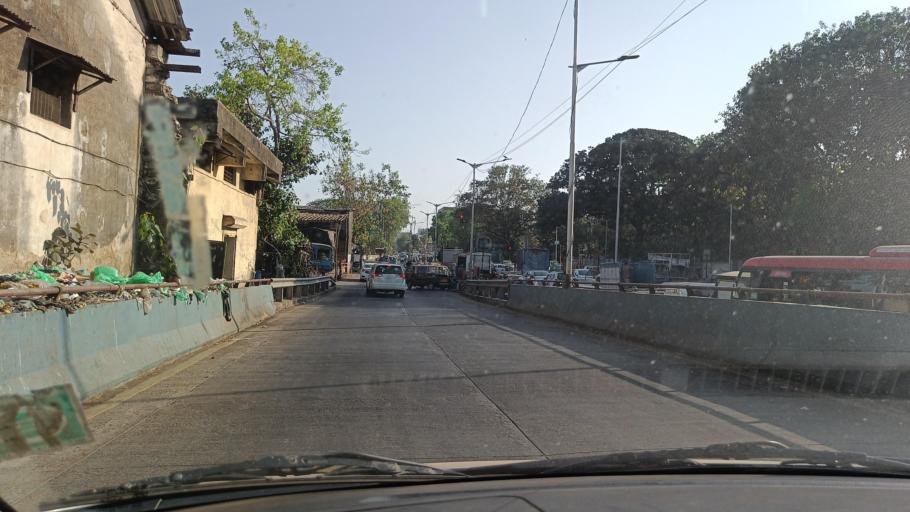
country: IN
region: Maharashtra
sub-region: Mumbai Suburban
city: Mumbai
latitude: 18.9583
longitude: 72.8431
